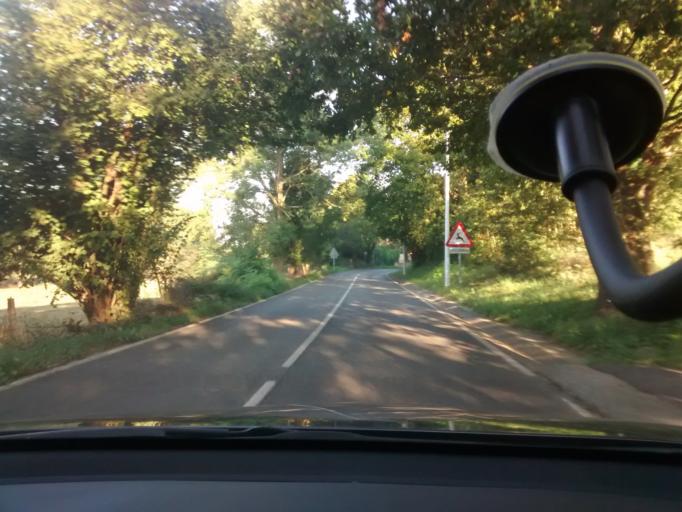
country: ES
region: Cantabria
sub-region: Provincia de Cantabria
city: Entrambasaguas
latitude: 43.3413
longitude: -3.6698
